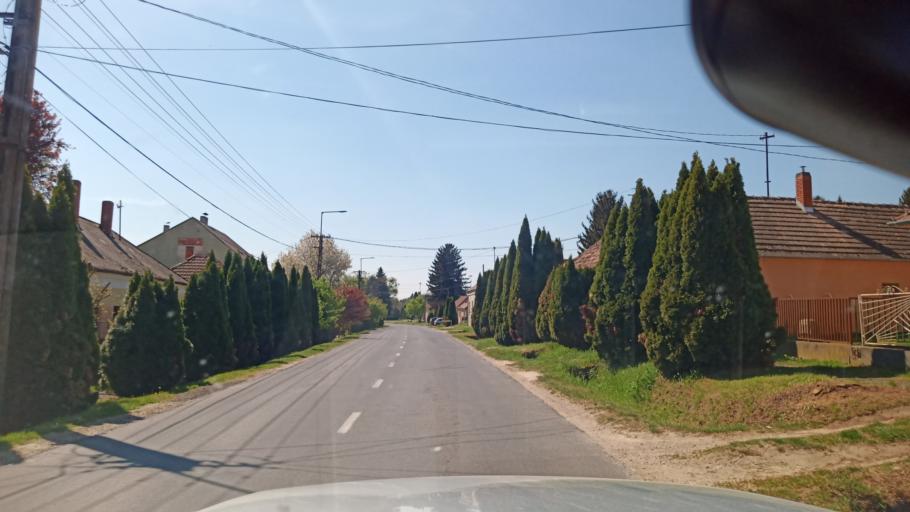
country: HU
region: Zala
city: Sarmellek
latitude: 46.7315
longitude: 17.1060
